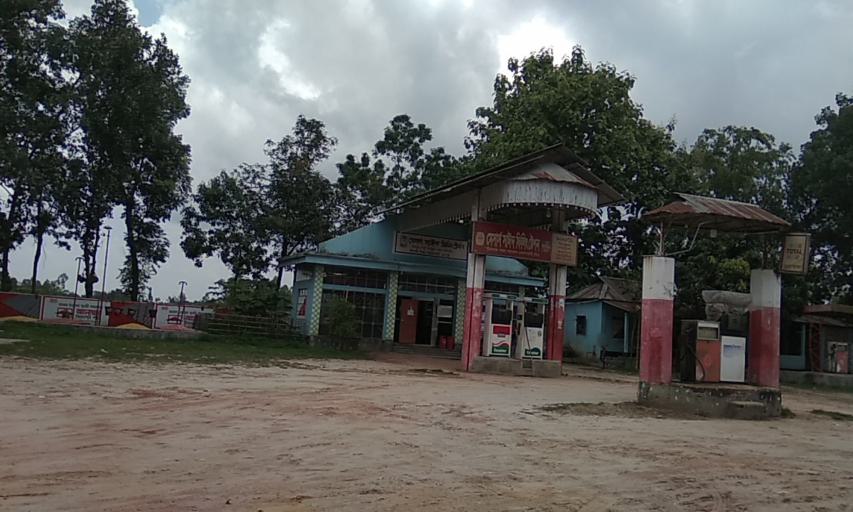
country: BD
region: Rangpur Division
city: Rangpur
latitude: 25.8019
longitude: 89.1834
